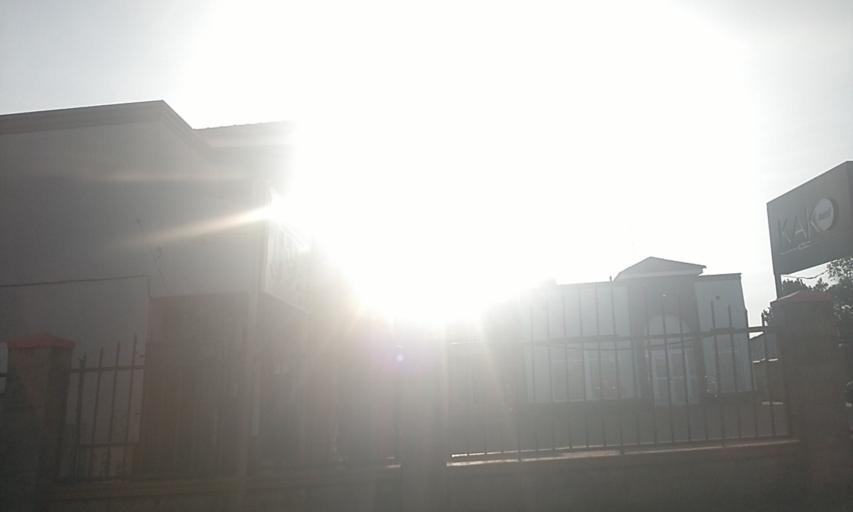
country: UG
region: Central Region
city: Kampala Central Division
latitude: 0.3670
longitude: 32.5976
